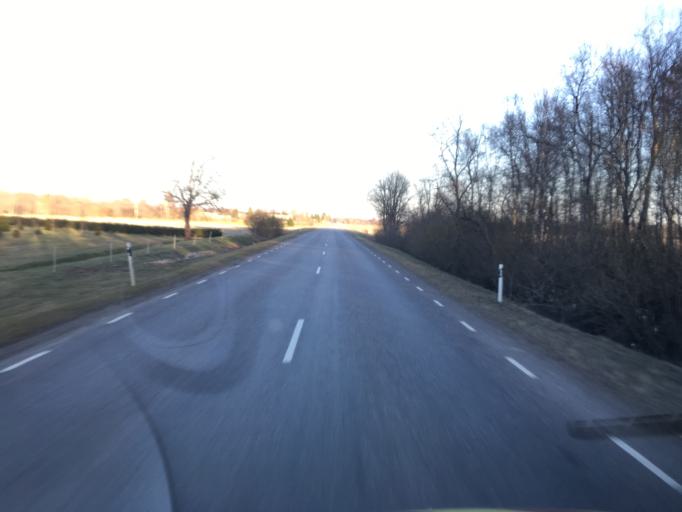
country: EE
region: Raplamaa
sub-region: Rapla vald
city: Rapla
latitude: 59.0858
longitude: 24.8149
